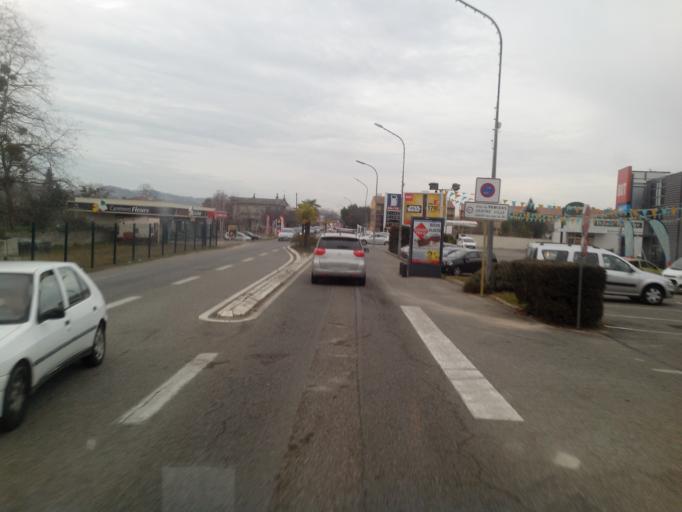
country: FR
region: Midi-Pyrenees
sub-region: Departement de l'Ariege
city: Saint-Jean-du-Falga
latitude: 43.1005
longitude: 1.6235
